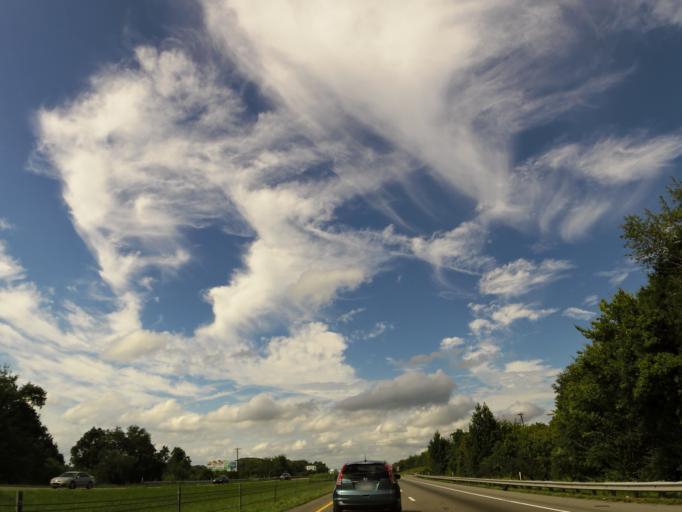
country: US
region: Tennessee
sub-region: Loudon County
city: Lenoir City
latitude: 35.8226
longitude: -84.2874
